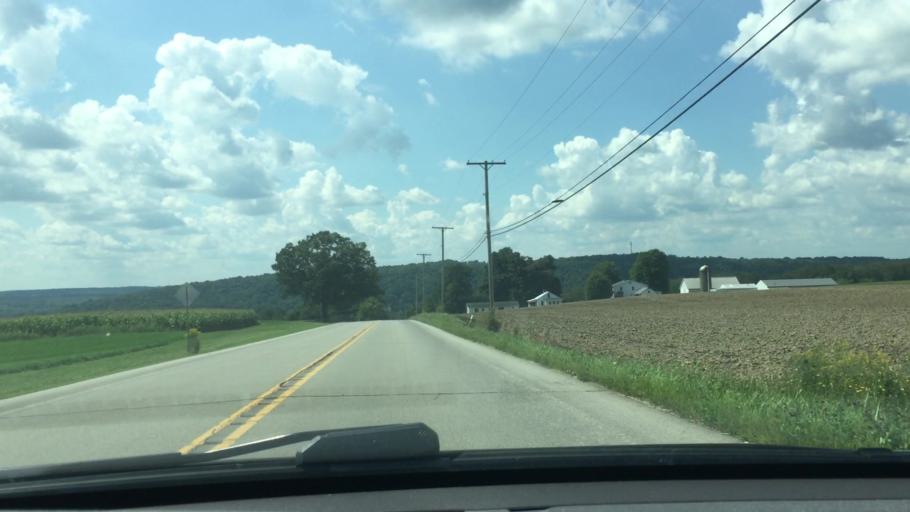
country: US
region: Pennsylvania
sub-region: Lawrence County
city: New Wilmington
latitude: 41.1146
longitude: -80.4176
